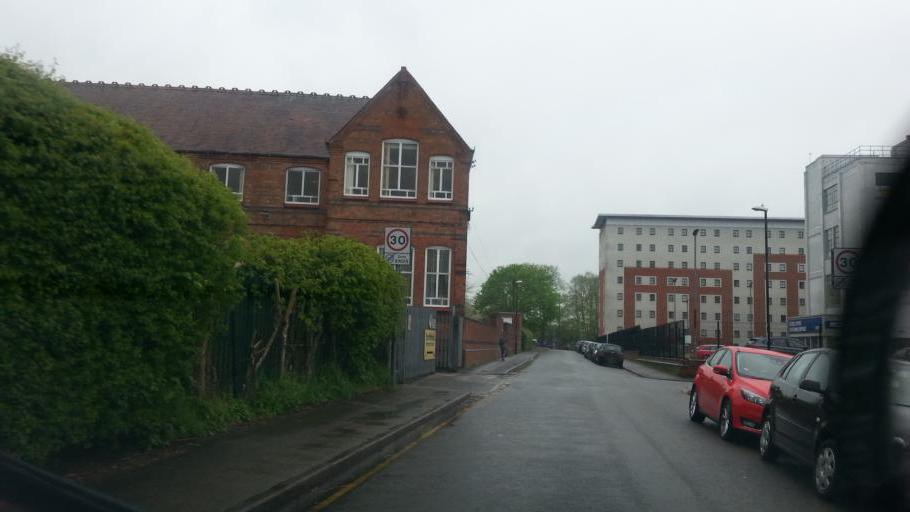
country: GB
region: England
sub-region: Coventry
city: Coventry
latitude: 52.4098
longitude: -1.4956
